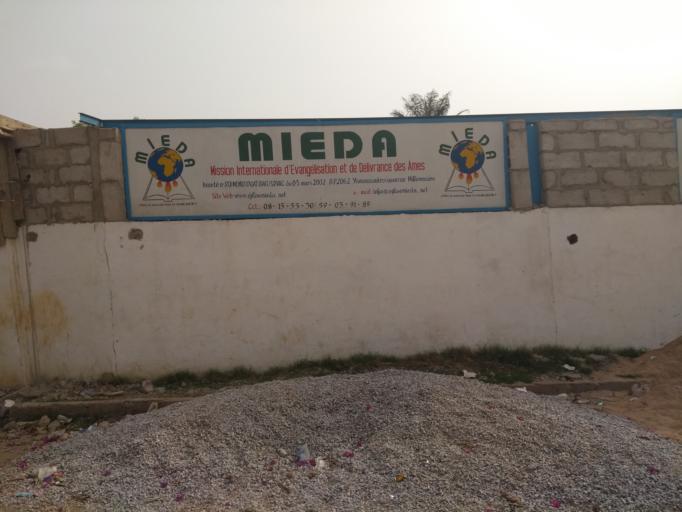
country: CI
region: Vallee du Bandama
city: Bouake
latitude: 7.6861
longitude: -5.0388
